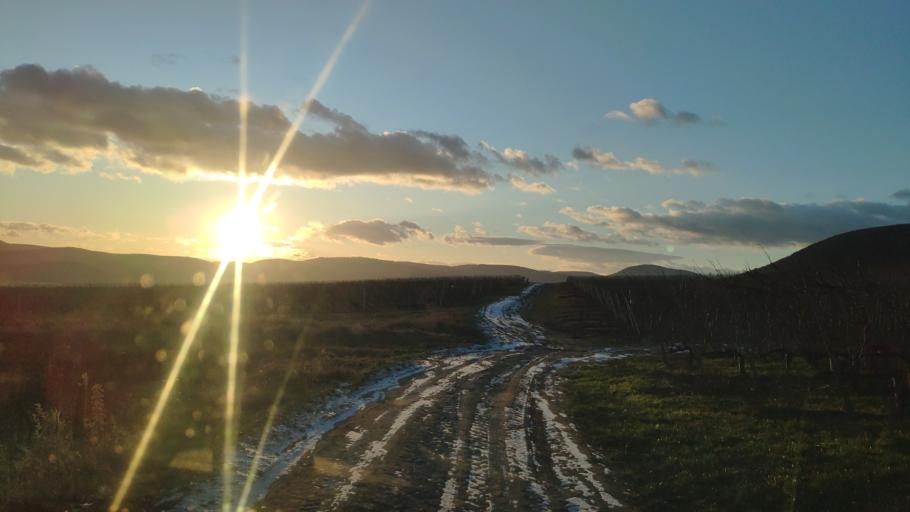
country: HU
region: Borsod-Abauj-Zemplen
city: Olaszliszka
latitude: 48.2755
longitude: 21.4140
